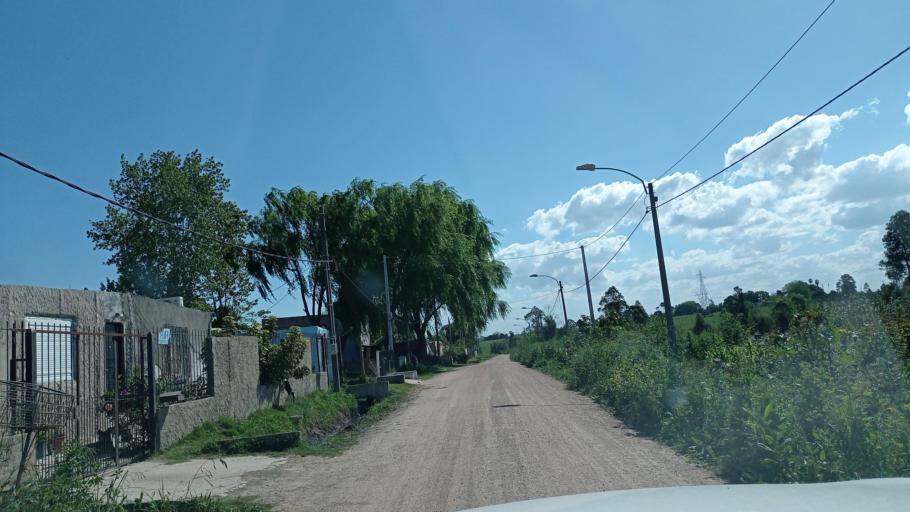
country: UY
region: Canelones
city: La Paz
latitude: -34.7804
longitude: -56.1577
